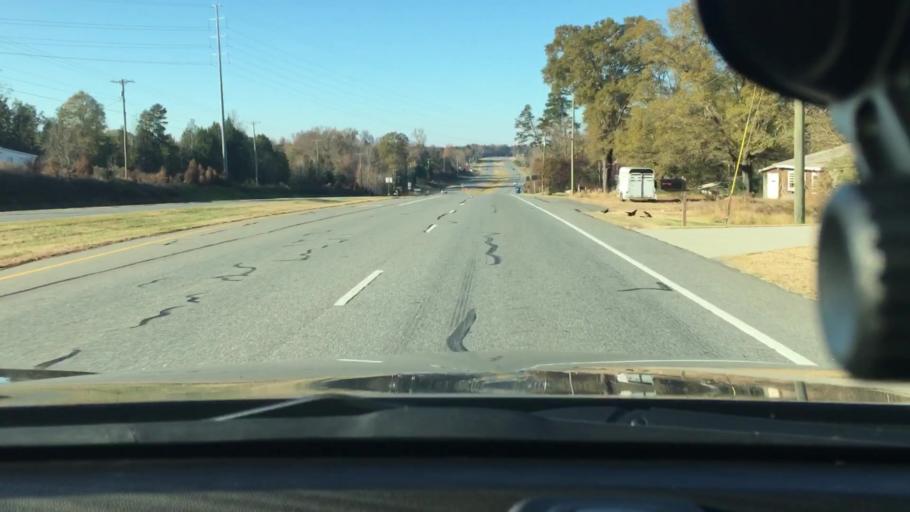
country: US
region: North Carolina
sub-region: Cabarrus County
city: Mount Pleasant
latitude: 35.3933
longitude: -80.4844
